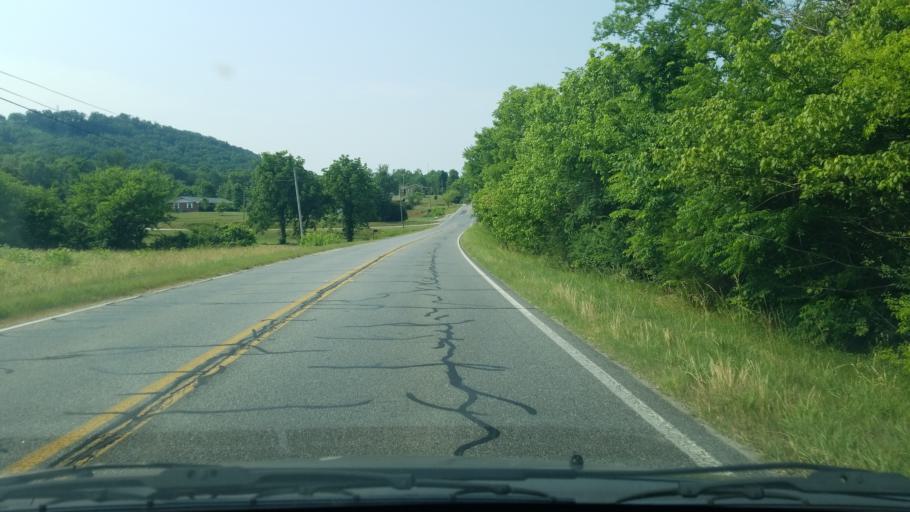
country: US
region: Georgia
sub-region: Catoosa County
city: Ringgold
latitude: 34.9284
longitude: -85.1038
